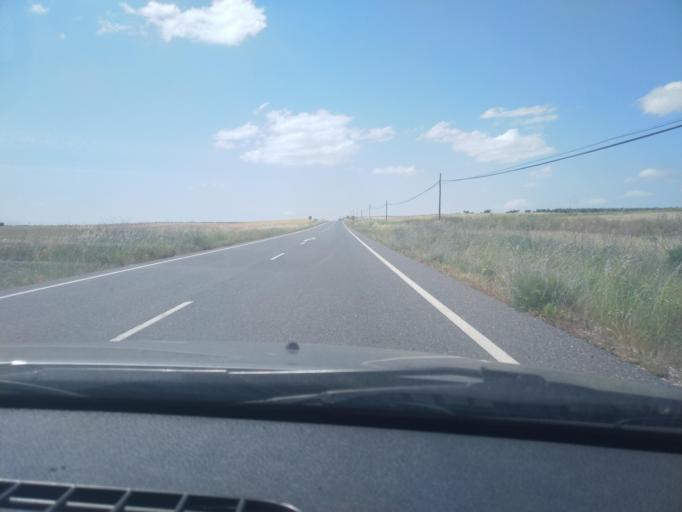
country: ES
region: Castille-La Mancha
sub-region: Province of Toledo
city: Casasbuenas
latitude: 39.7626
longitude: -4.1345
